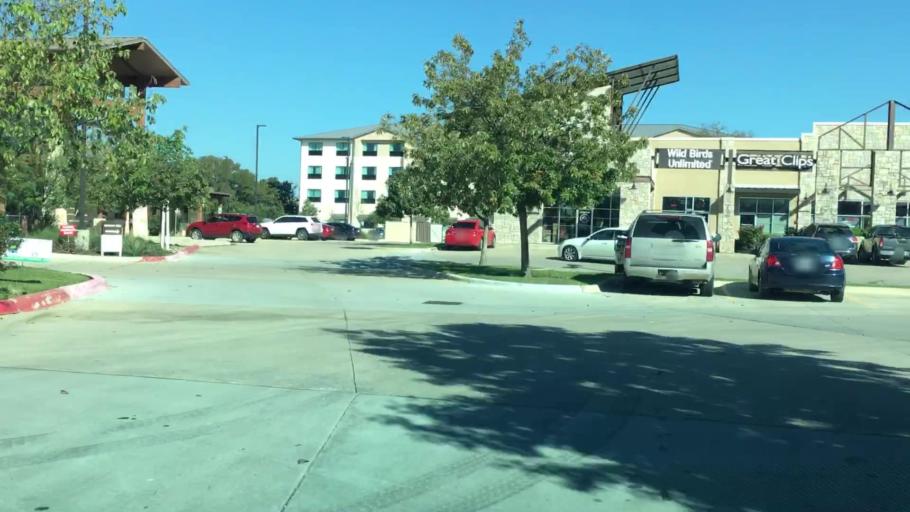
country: US
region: Texas
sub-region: Hays County
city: Dripping Springs
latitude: 30.1923
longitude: -98.0837
